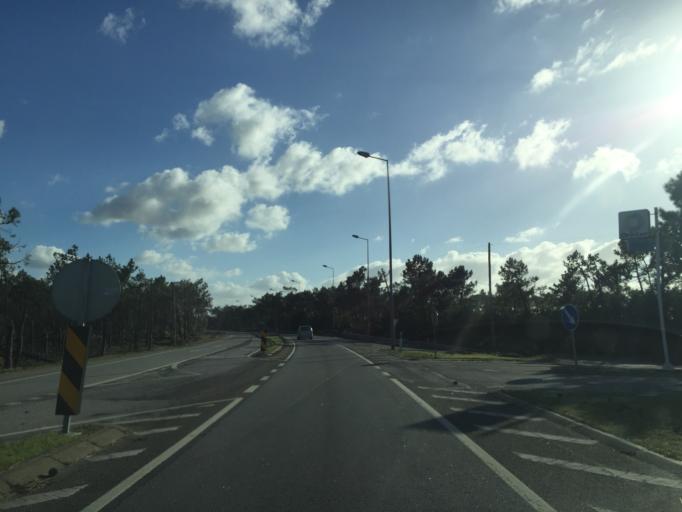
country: PT
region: Coimbra
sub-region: Figueira da Foz
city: Figueira da Foz
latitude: 40.1189
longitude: -8.8559
